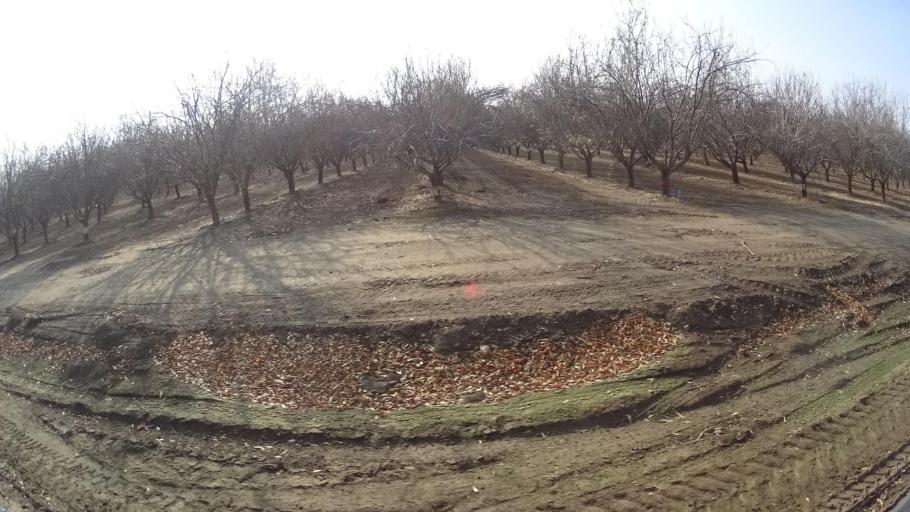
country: US
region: California
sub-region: Kern County
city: Lebec
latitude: 34.9930
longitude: -118.8511
